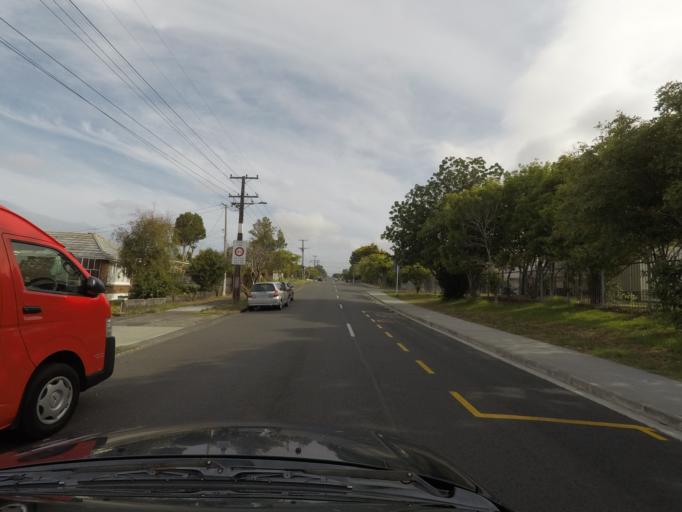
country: NZ
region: Auckland
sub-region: Auckland
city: Waitakere
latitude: -36.8991
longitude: 174.6671
